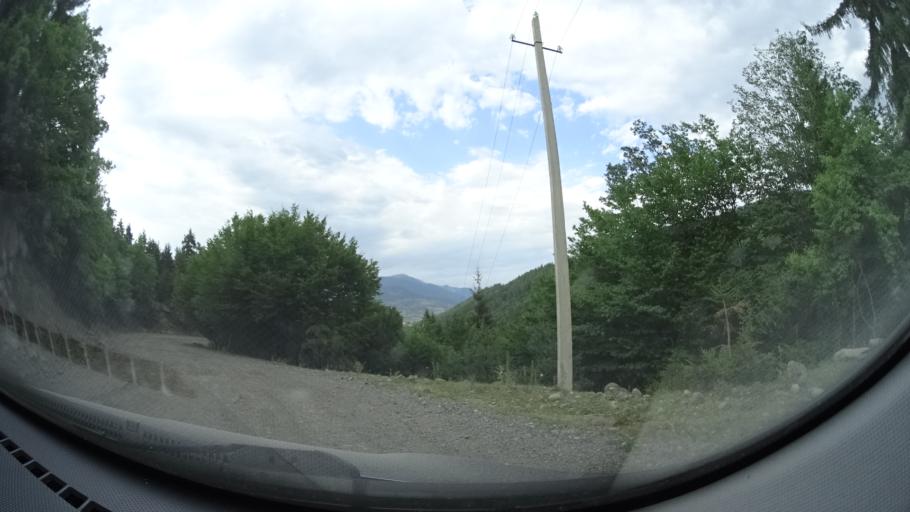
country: GE
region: Samtskhe-Javakheti
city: Adigeni
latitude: 41.6686
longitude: 42.6347
